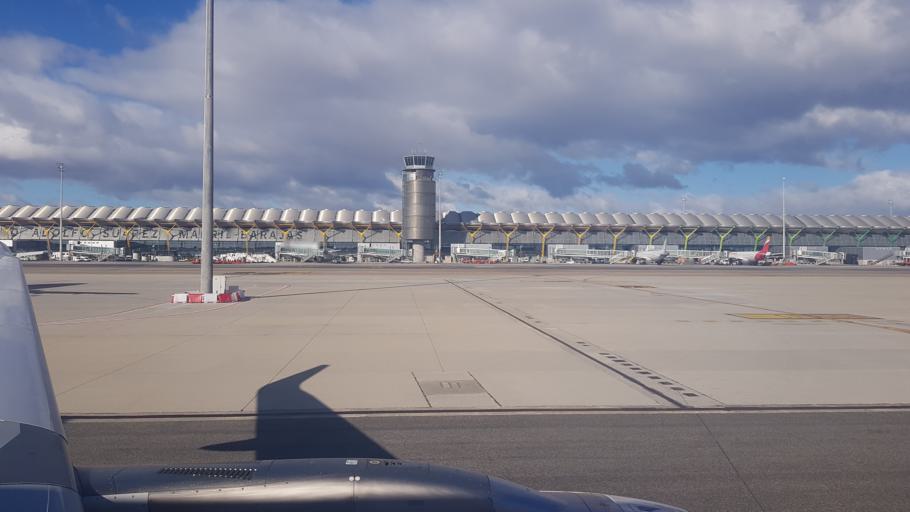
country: ES
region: Madrid
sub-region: Provincia de Madrid
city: Barajas de Madrid
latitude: 40.4921
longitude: -3.5865
